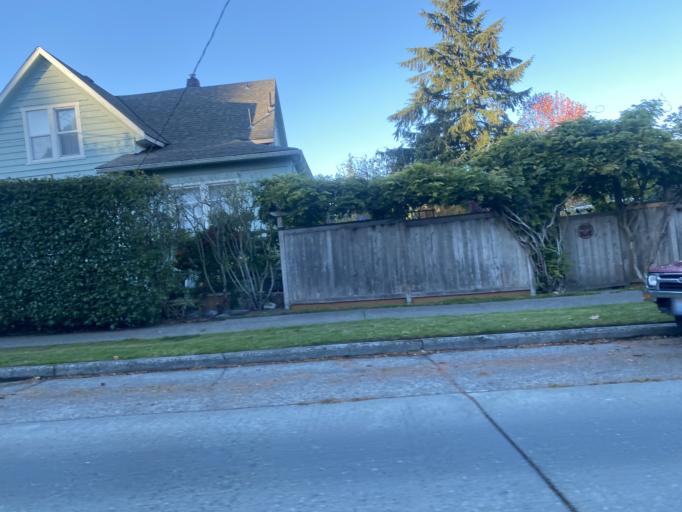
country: US
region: Washington
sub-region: King County
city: Seattle
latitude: 47.6541
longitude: -122.4020
